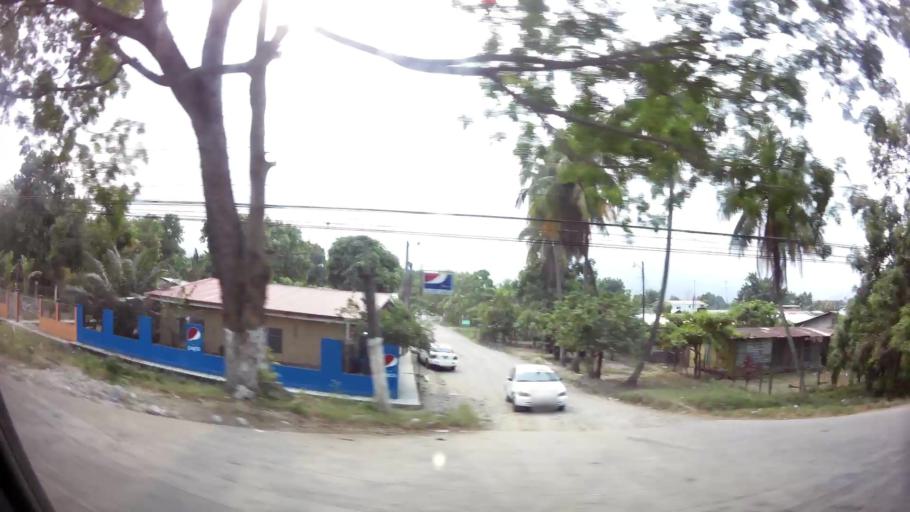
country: HN
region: Yoro
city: El Progreso
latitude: 15.4248
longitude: -87.7985
